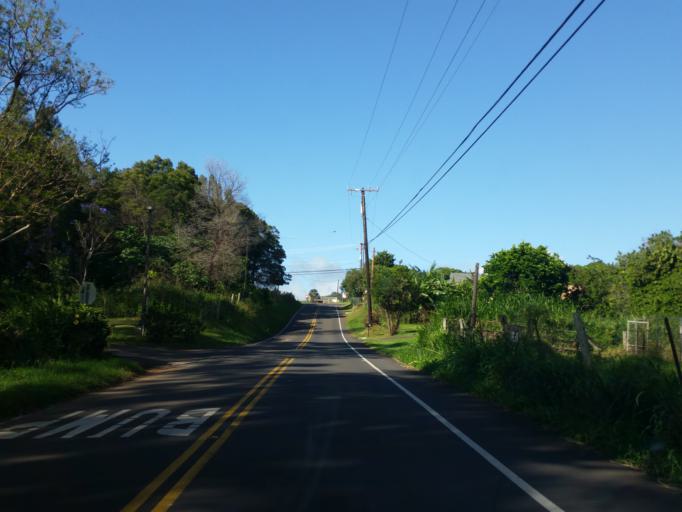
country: US
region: Hawaii
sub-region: Maui County
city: Makawao
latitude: 20.8388
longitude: -156.3086
